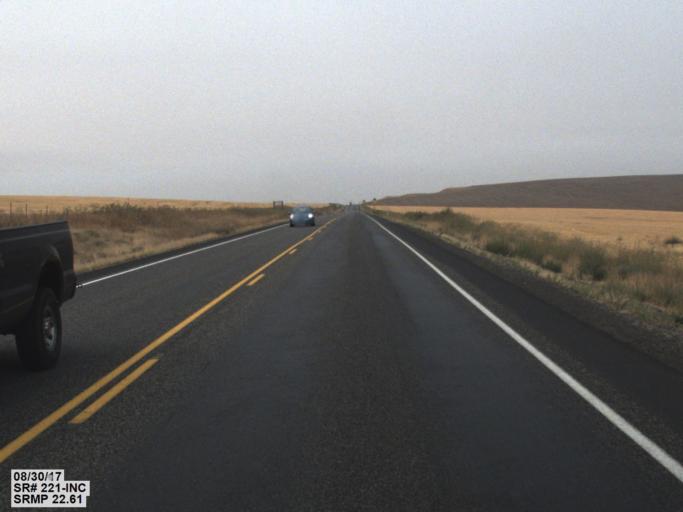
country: US
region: Washington
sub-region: Benton County
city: Prosser
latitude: 46.1931
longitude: -119.7059
